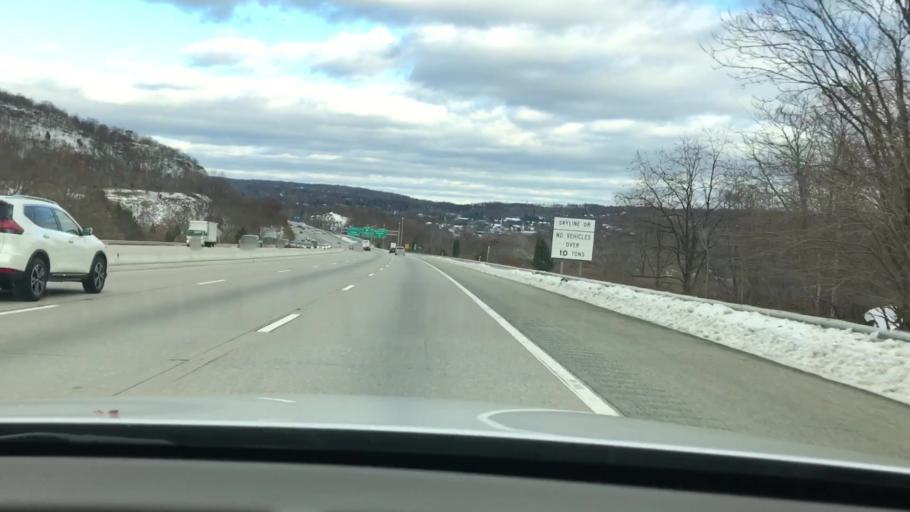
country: US
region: New Jersey
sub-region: Bergen County
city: Oakland
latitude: 41.0237
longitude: -74.2672
